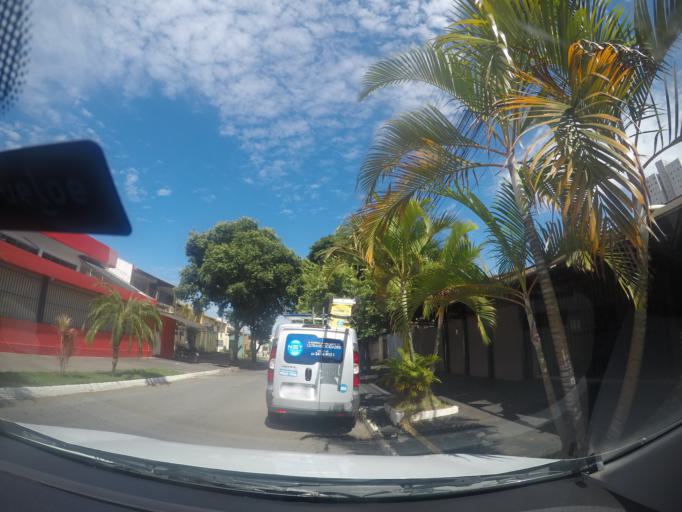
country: BR
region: Goias
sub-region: Goiania
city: Goiania
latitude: -16.7224
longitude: -49.2669
